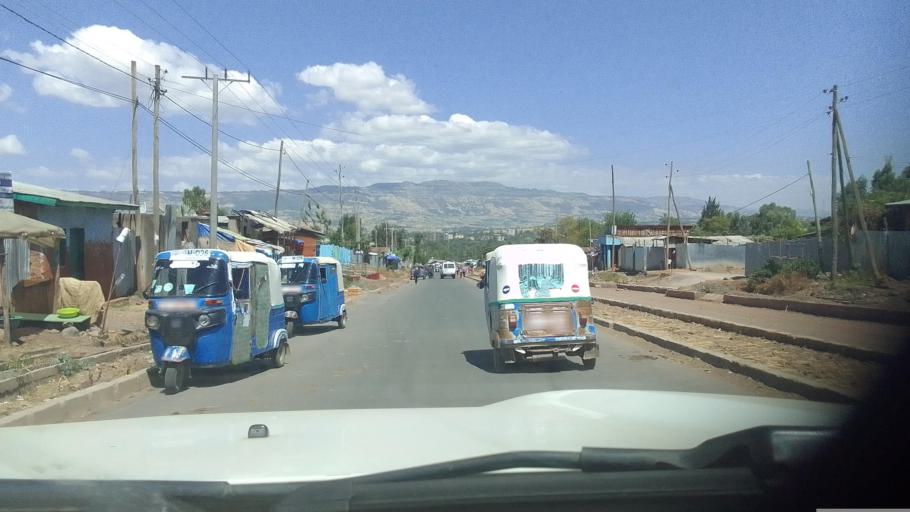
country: ET
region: Oromiya
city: Hagere Hiywet
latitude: 8.9700
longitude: 37.8494
